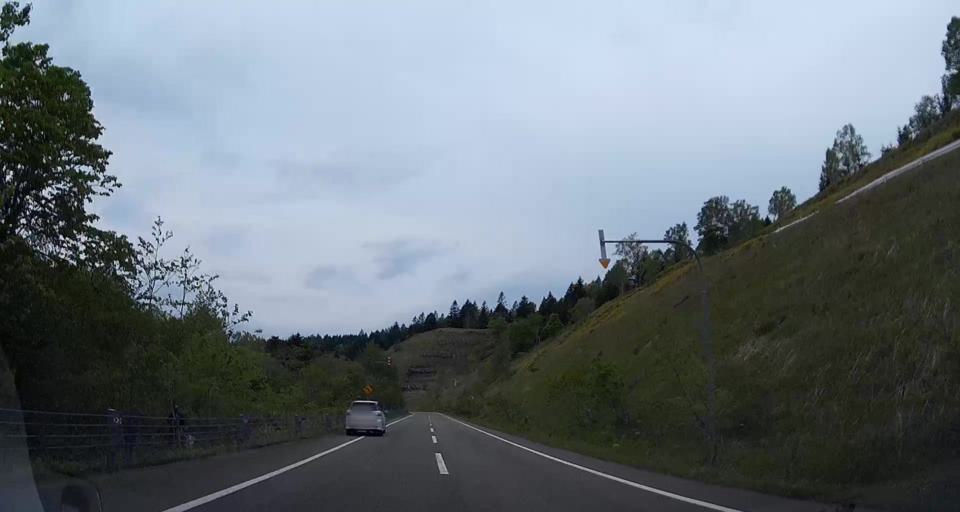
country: JP
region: Hokkaido
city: Shiraoi
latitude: 42.6775
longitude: 141.1284
